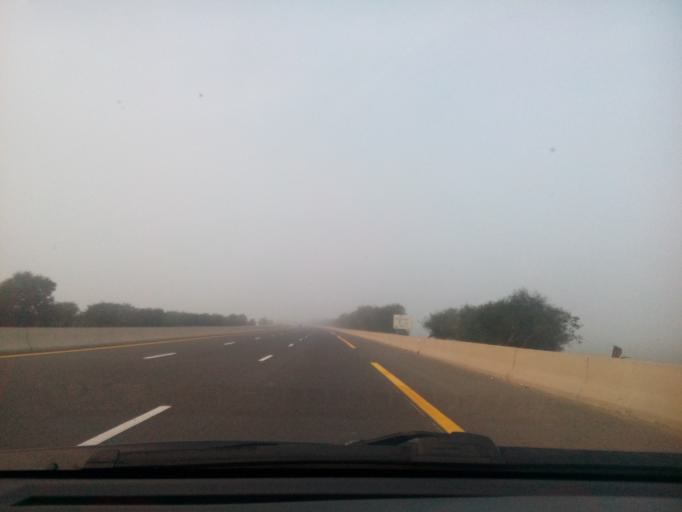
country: DZ
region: Relizane
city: Relizane
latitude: 35.7984
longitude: 0.5110
